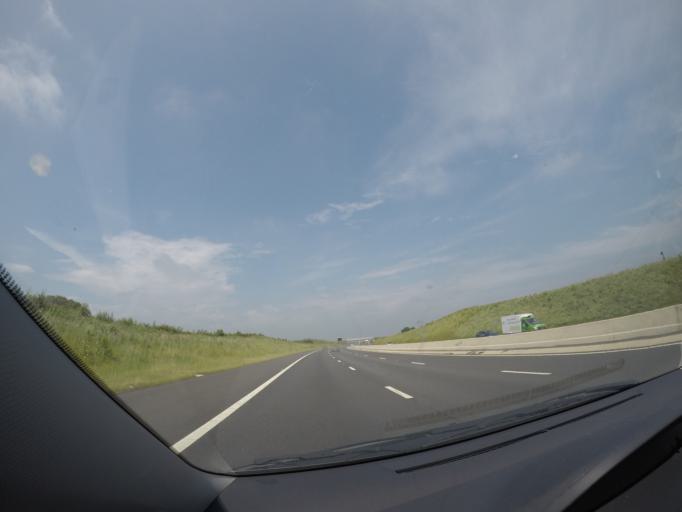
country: GB
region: England
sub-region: North Yorkshire
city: Catterick
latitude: 54.3657
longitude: -1.6326
